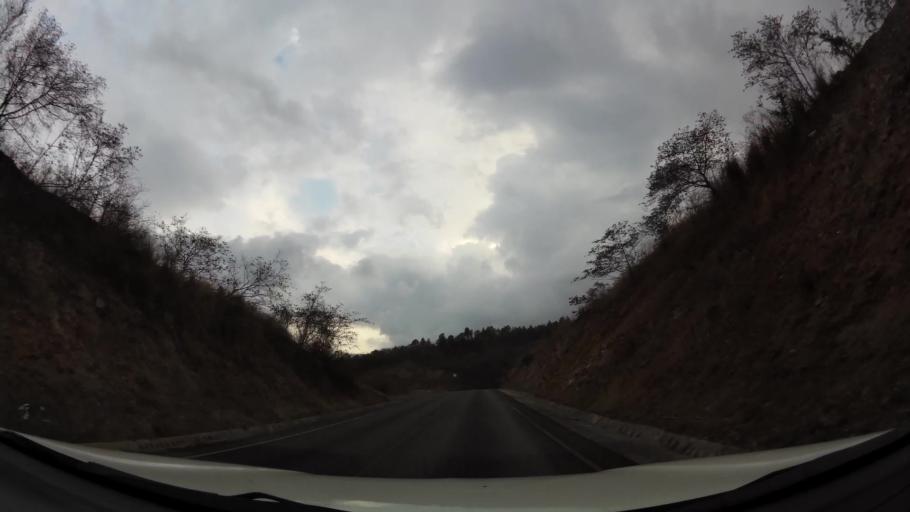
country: NI
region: Jinotega
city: Jinotega
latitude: 13.0208
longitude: -86.0040
